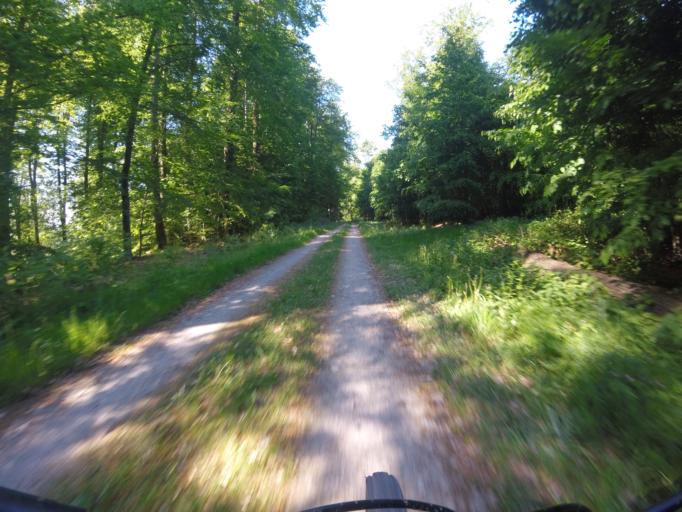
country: DE
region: Baden-Wuerttemberg
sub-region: Regierungsbezirk Stuttgart
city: Aspach
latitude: 49.0043
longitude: 9.4194
